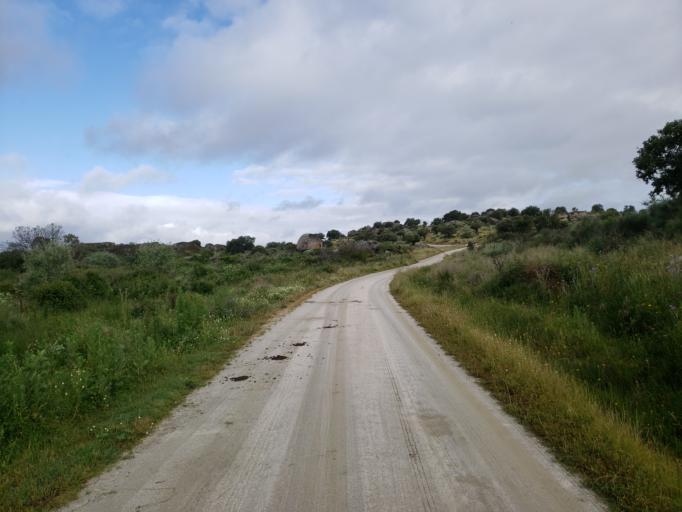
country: ES
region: Extremadura
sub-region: Provincia de Caceres
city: Malpartida de Caceres
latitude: 39.4261
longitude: -6.4923
